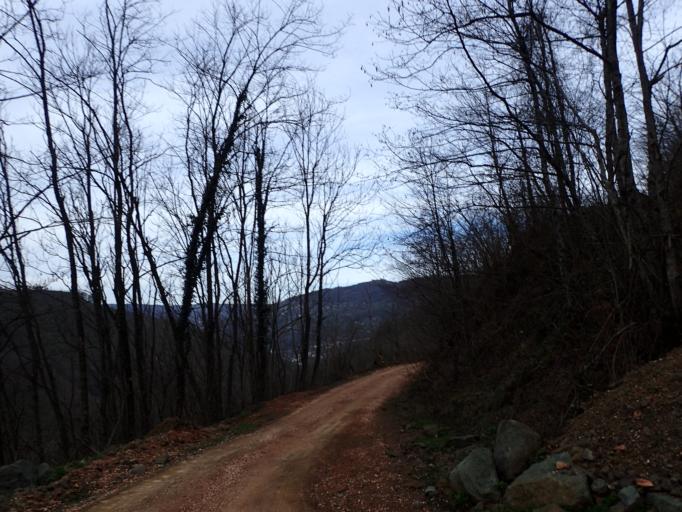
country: TR
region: Ordu
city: Camas
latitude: 40.8876
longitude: 37.5109
